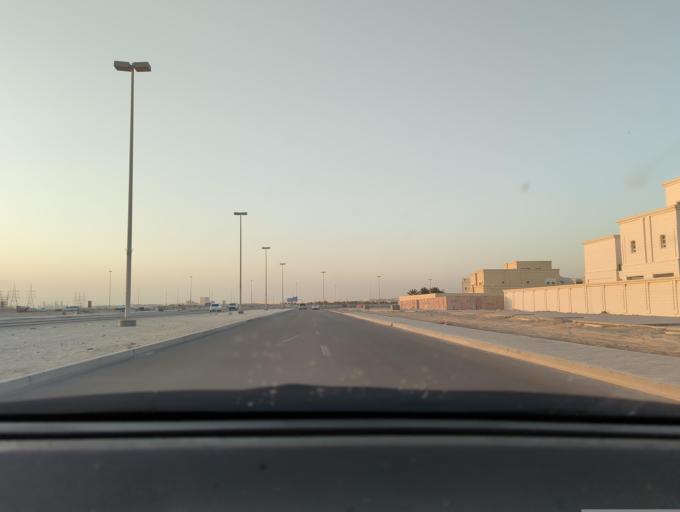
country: AE
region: Abu Dhabi
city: Abu Dhabi
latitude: 24.3102
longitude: 54.5330
